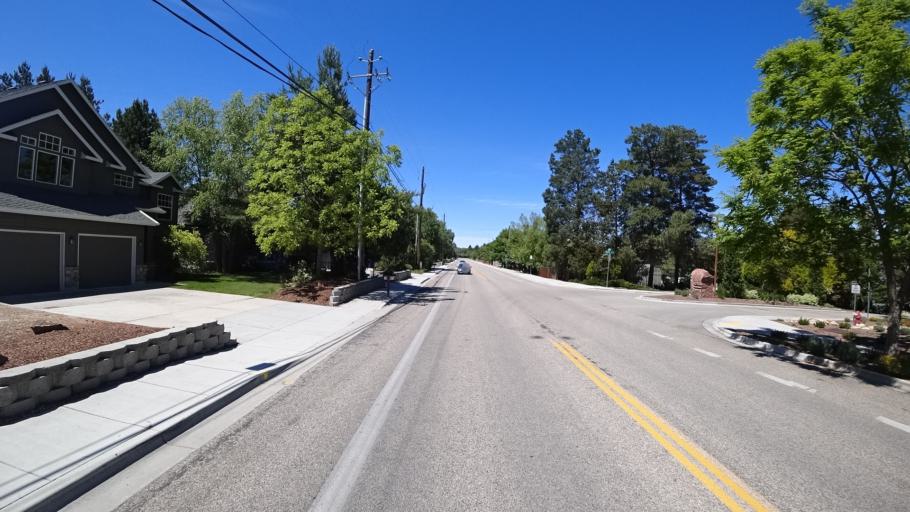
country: US
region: Idaho
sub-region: Ada County
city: Boise
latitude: 43.5641
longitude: -116.1349
